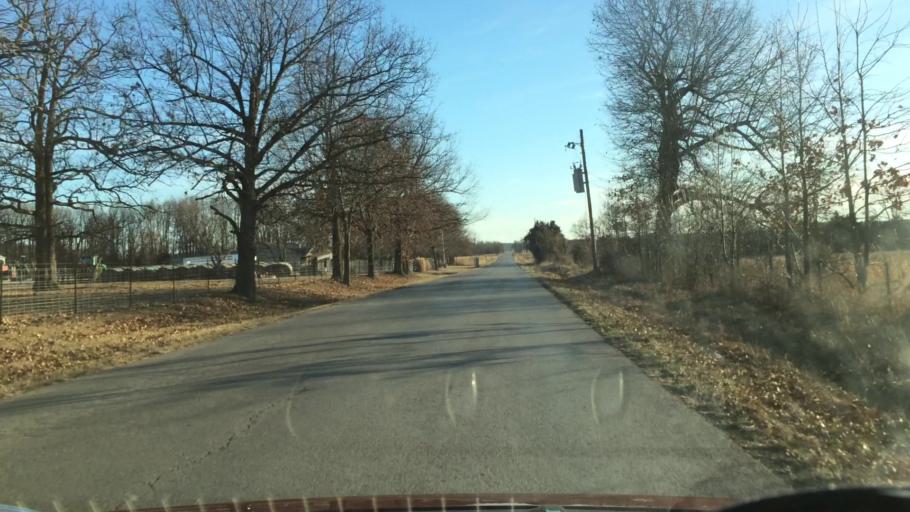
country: US
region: Missouri
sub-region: Webster County
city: Marshfield
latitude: 37.3392
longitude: -92.9838
